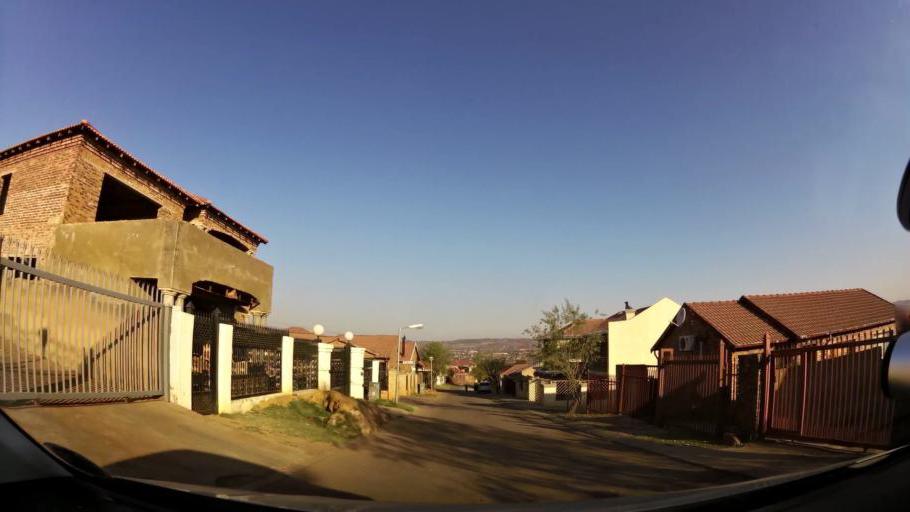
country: ZA
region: Gauteng
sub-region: City of Tshwane Metropolitan Municipality
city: Pretoria
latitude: -25.7336
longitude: 28.1183
